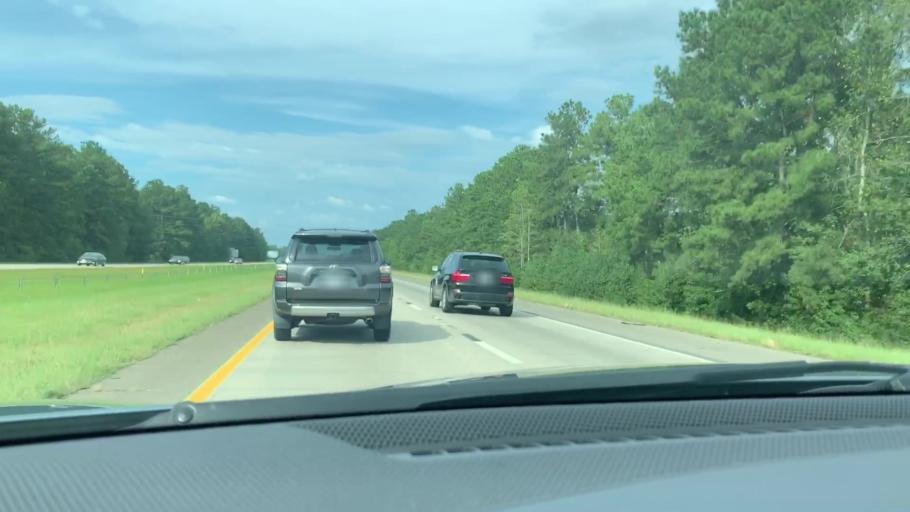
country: US
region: South Carolina
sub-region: Colleton County
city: Walterboro
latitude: 32.9480
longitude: -80.6828
